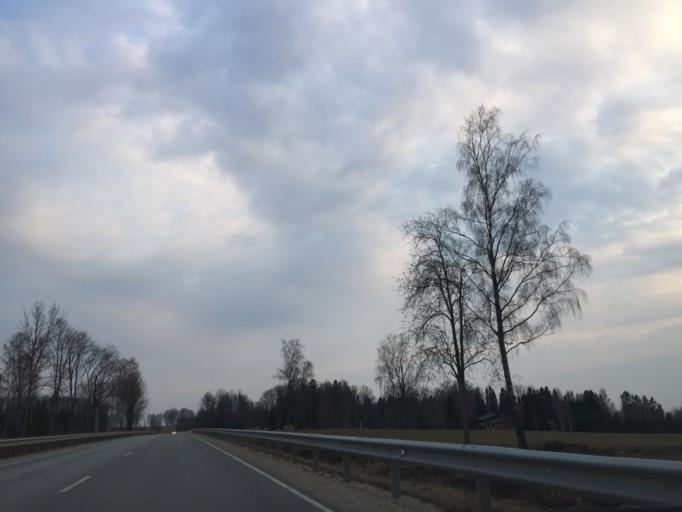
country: LV
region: Vecpiebalga
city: Vecpiebalga
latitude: 57.1509
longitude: 25.6653
